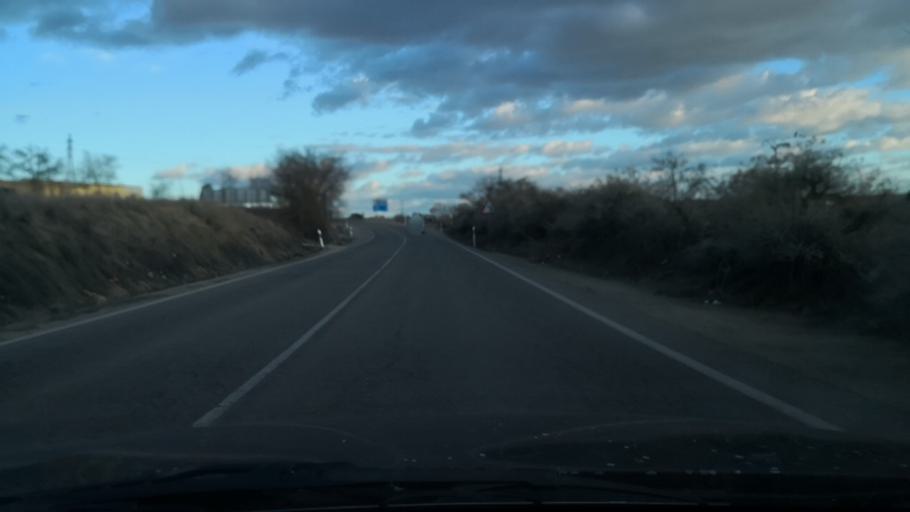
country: ES
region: Castille and Leon
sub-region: Provincia de Valladolid
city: Medina del Campo
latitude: 41.3117
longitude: -4.9031
